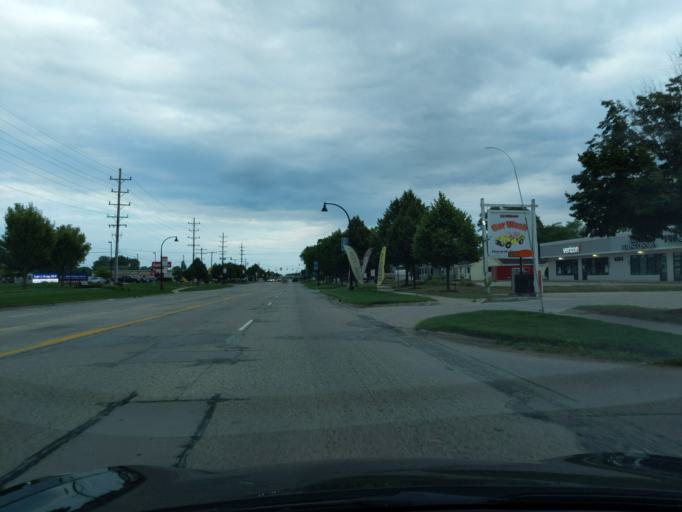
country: US
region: Michigan
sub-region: Isabella County
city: Mount Pleasant
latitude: 43.6117
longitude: -84.7517
